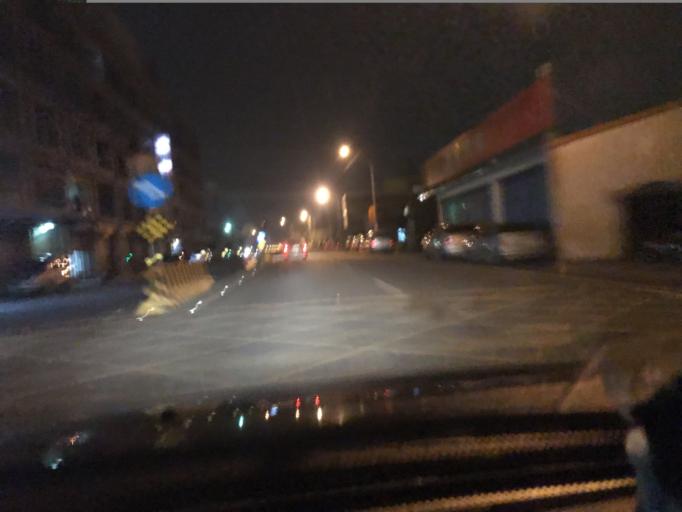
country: TW
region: Taiwan
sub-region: Hsinchu
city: Zhubei
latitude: 24.7956
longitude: 121.0563
